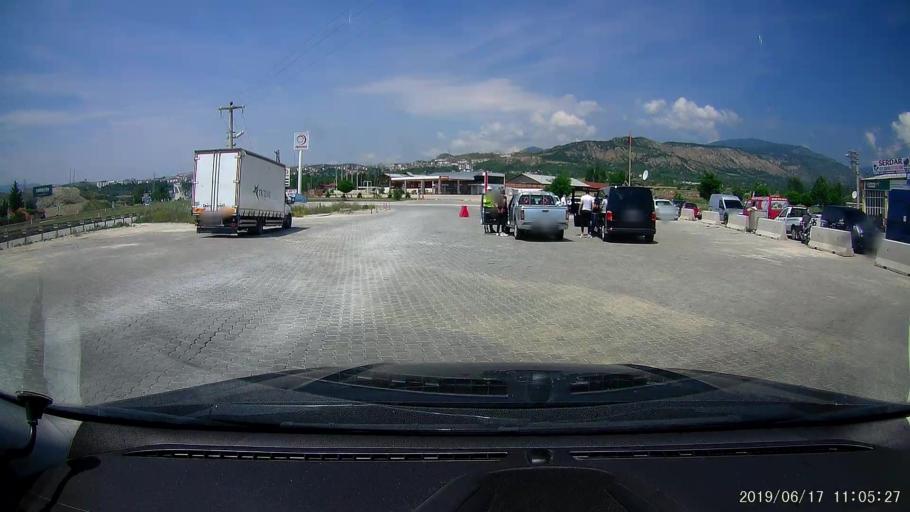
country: TR
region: Kastamonu
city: Tosya
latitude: 41.0178
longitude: 34.0764
